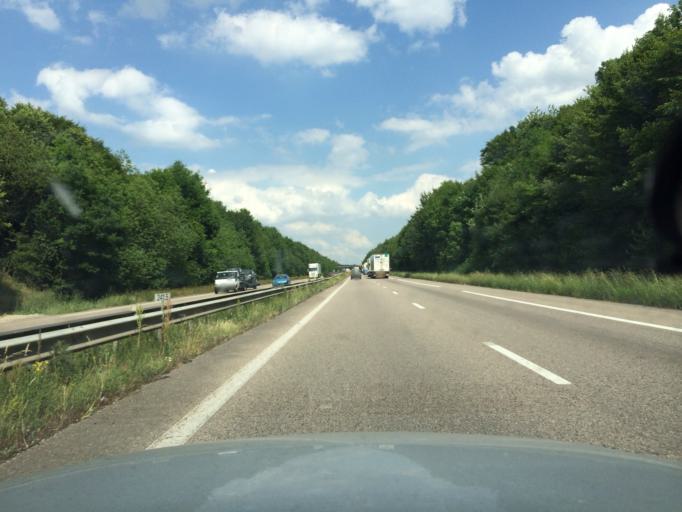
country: FR
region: Lorraine
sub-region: Departement de Meurthe-et-Moselle
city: Velaine-en-Haye
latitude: 48.6896
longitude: 6.0244
